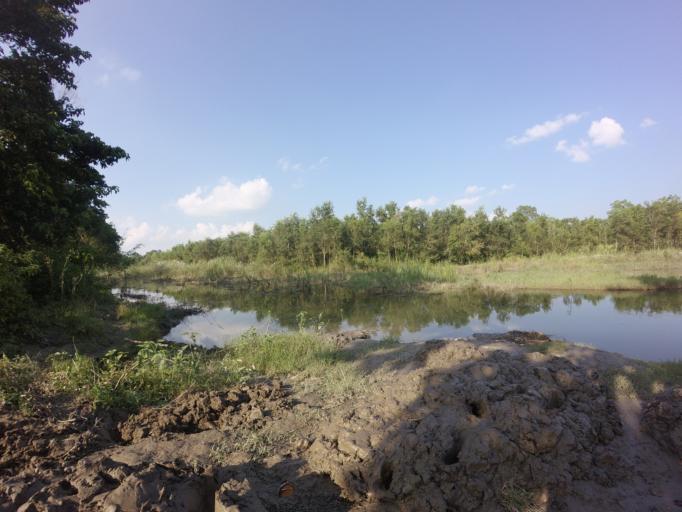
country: NP
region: Far Western
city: Tikapur
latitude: 28.4430
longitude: 81.0784
